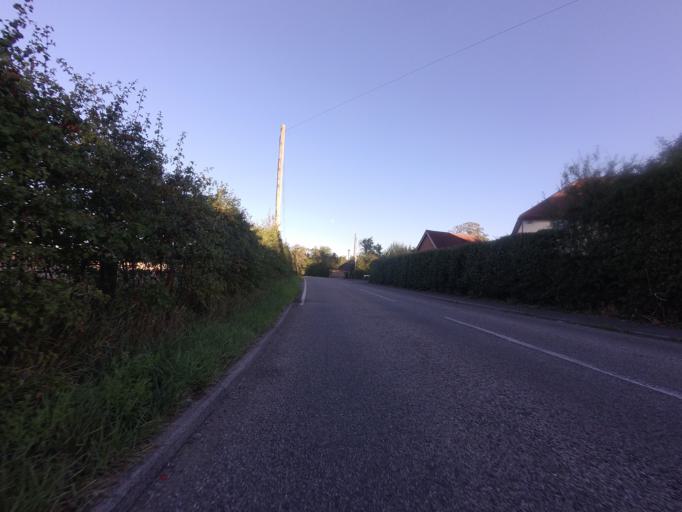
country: GB
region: England
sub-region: Kent
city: Sturry
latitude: 51.3253
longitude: 1.2021
